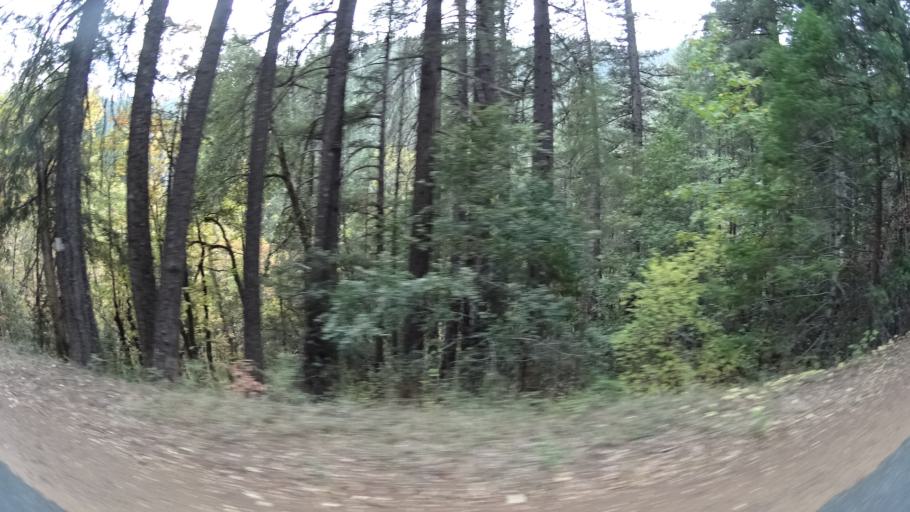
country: US
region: California
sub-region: Siskiyou County
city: Happy Camp
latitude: 41.7519
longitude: -123.3631
